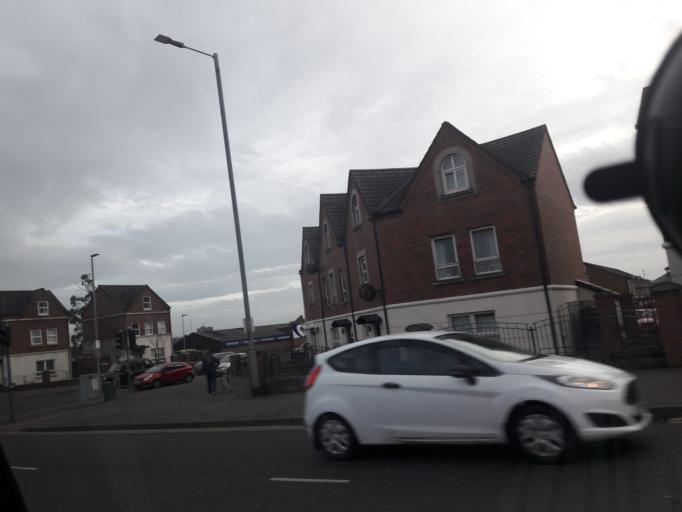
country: GB
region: Northern Ireland
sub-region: City of Belfast
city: Belfast
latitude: 54.6096
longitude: -5.9463
